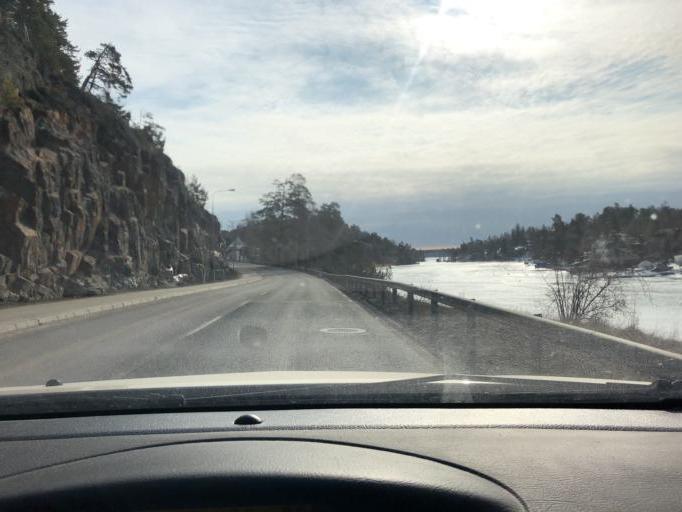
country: SE
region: Stockholm
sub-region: Nacka Kommun
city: Boo
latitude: 59.3344
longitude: 18.3015
